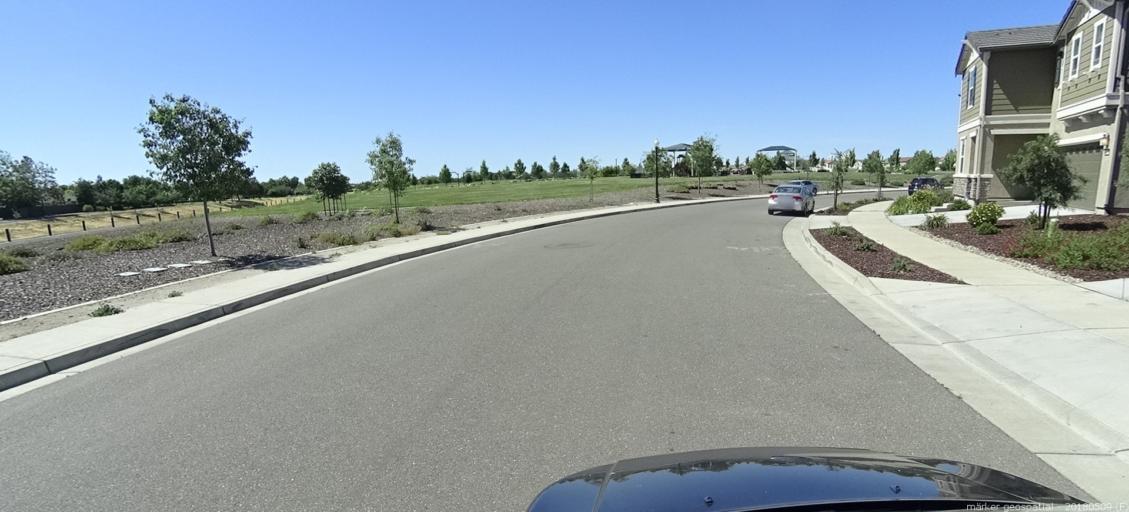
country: US
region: California
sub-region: Sacramento County
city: Elverta
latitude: 38.6703
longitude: -121.5249
